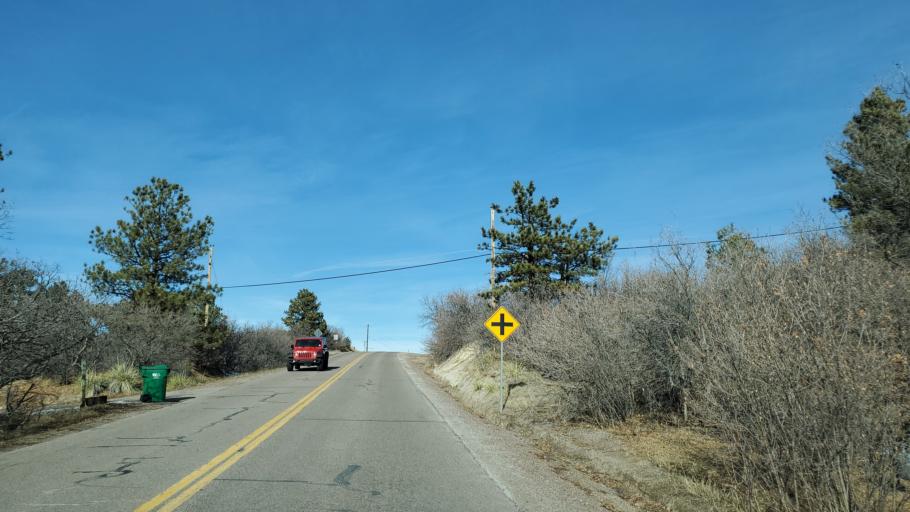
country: US
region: Colorado
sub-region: Douglas County
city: Castle Pines
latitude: 39.4464
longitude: -104.8719
